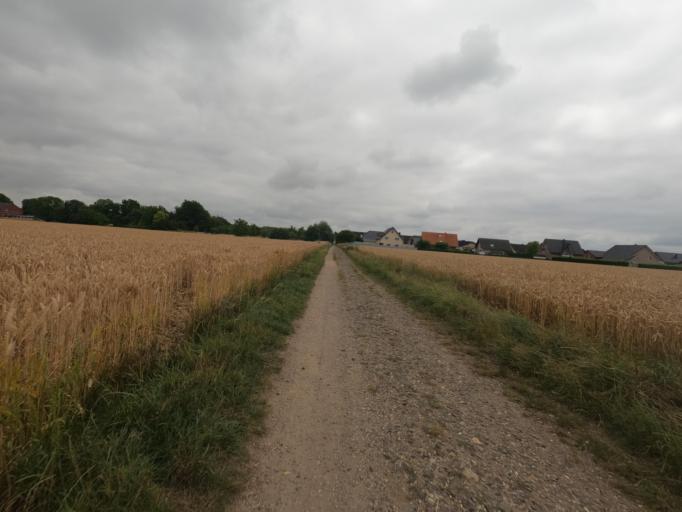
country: DE
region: North Rhine-Westphalia
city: Geilenkirchen
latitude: 50.9783
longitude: 6.1153
